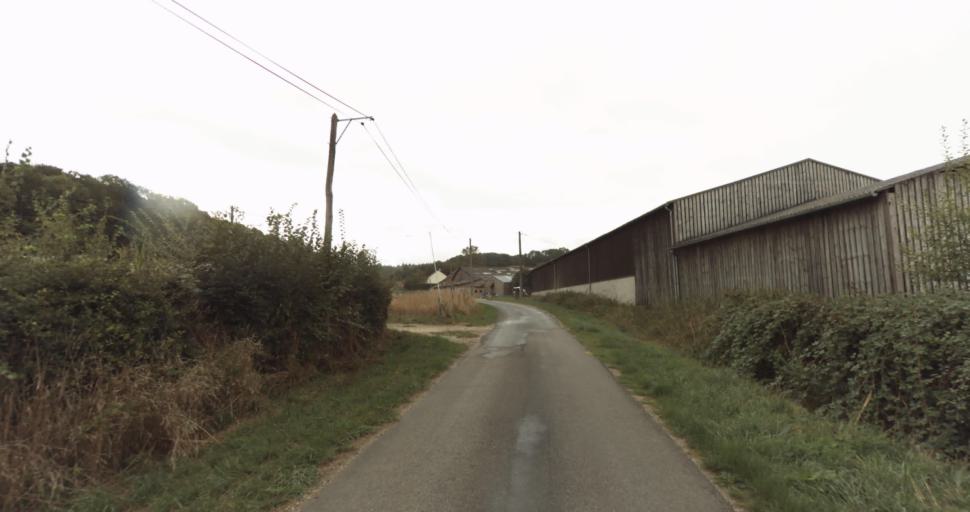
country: FR
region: Lower Normandy
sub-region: Departement de l'Orne
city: Gace
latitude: 48.8021
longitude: 0.3251
